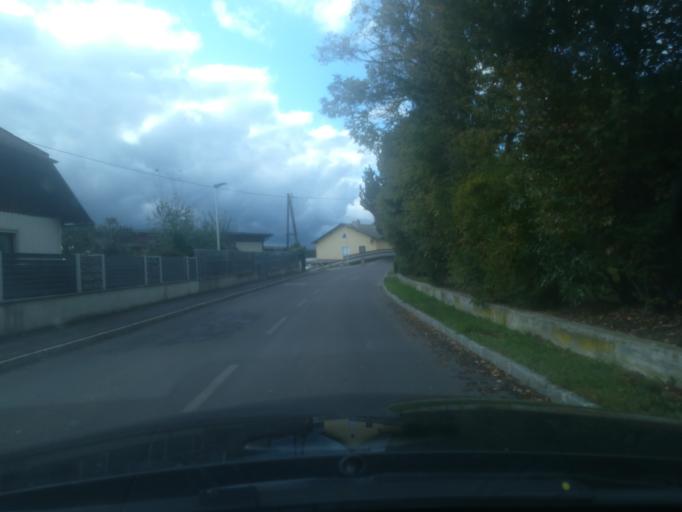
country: AT
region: Upper Austria
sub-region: Politischer Bezirk Urfahr-Umgebung
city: Herzogsdorf
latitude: 48.4278
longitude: 14.1293
